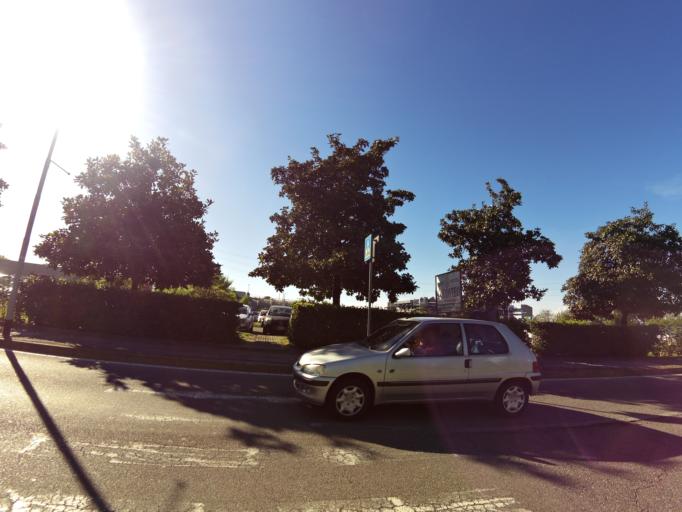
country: IT
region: Lombardy
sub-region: Citta metropolitana di Milano
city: Rozzano
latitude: 45.3986
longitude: 9.1454
